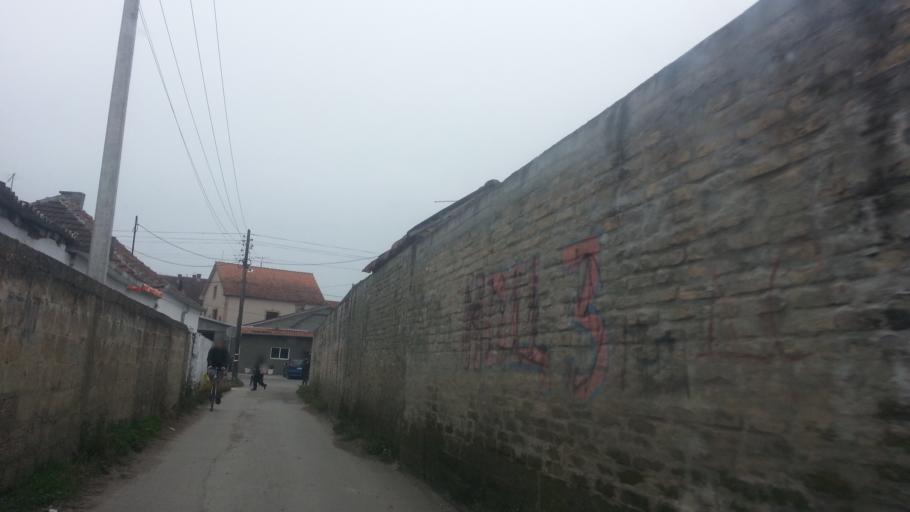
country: RS
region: Autonomna Pokrajina Vojvodina
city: Nova Pazova
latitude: 44.9516
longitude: 20.2182
